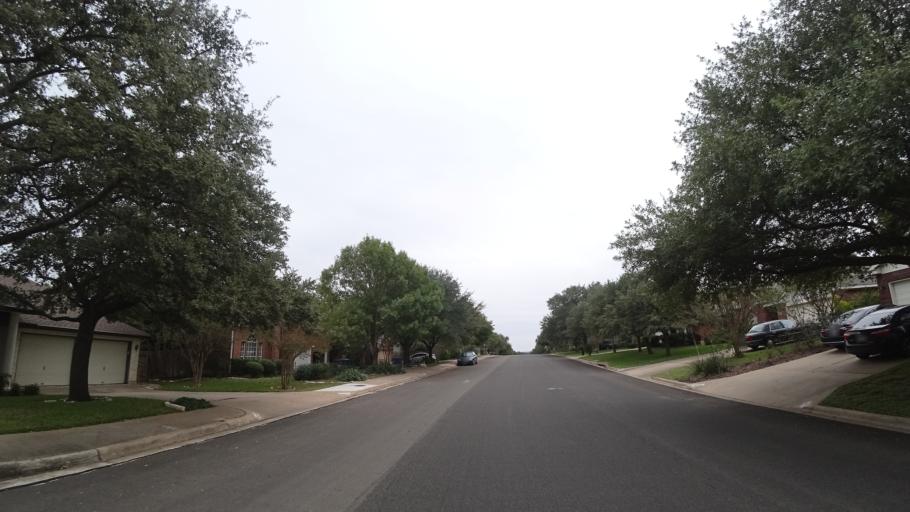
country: US
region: Texas
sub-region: Travis County
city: Shady Hollow
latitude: 30.1870
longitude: -97.8907
